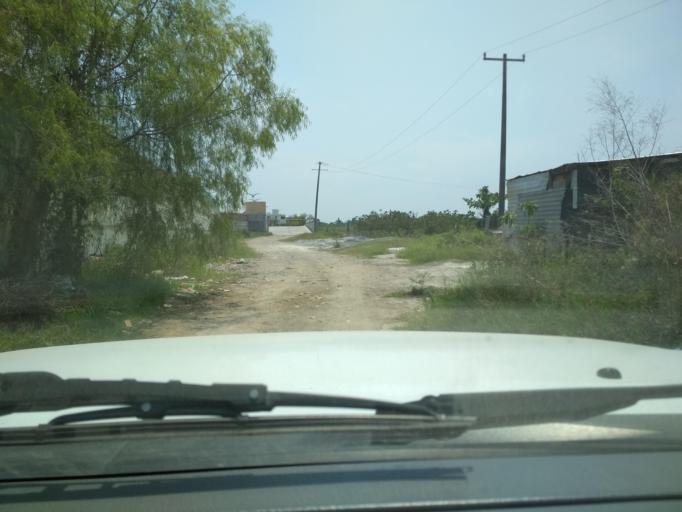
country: MX
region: Veracruz
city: Boca del Rio
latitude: 19.1069
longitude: -96.1263
